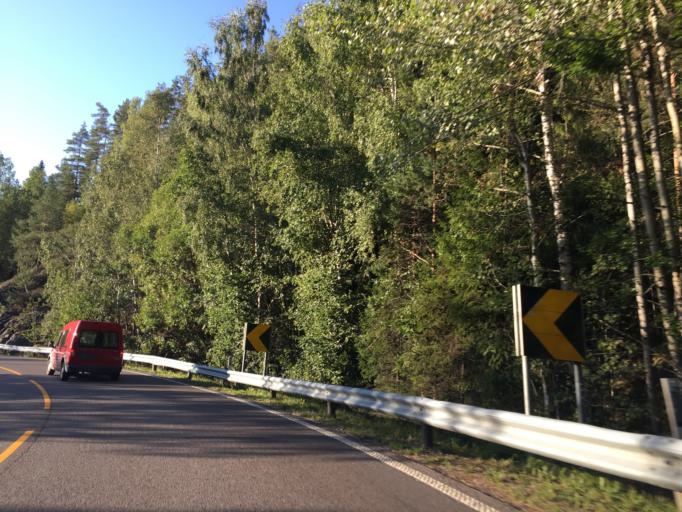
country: NO
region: Akershus
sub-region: Enebakk
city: Flateby
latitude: 59.8125
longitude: 11.2492
